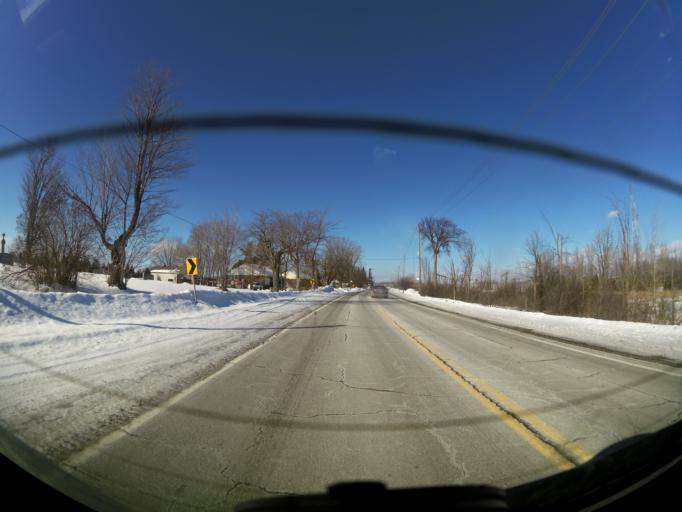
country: CA
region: Ontario
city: Ottawa
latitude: 45.3852
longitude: -75.5959
